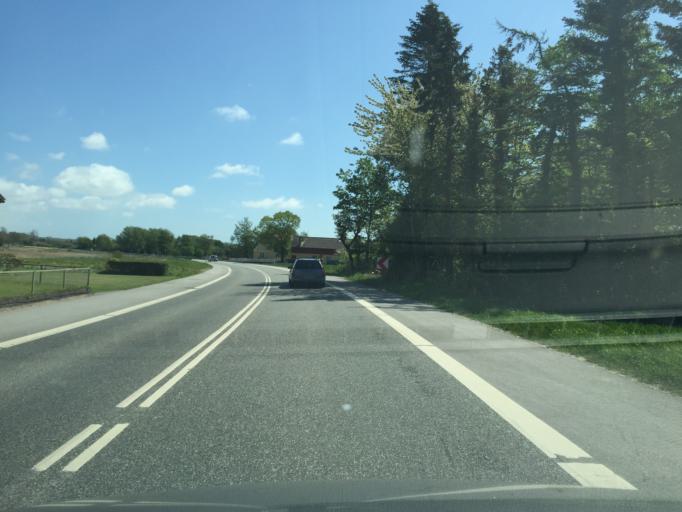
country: DK
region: Zealand
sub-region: Vordingborg Kommune
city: Stege
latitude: 54.9672
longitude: 12.2027
